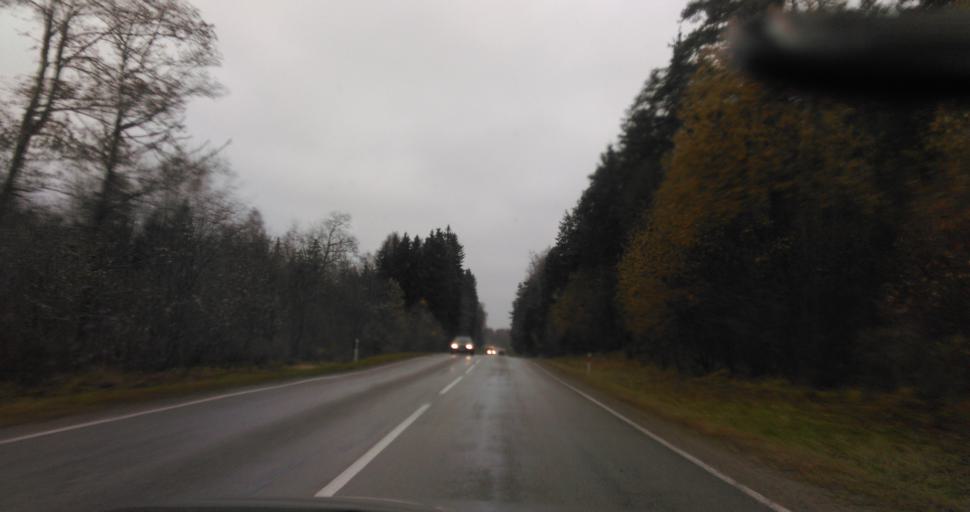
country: LT
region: Panevezys
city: Rokiskis
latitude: 55.8665
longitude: 25.5452
